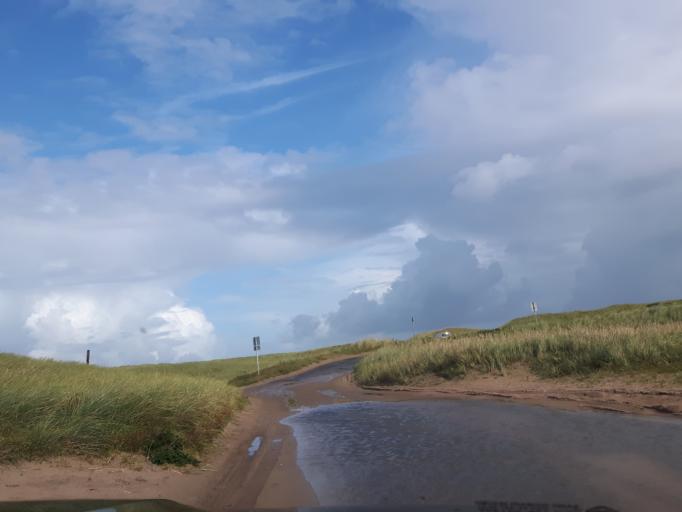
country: DK
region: North Denmark
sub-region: Thisted Kommune
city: Hanstholm
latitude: 57.0864
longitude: 8.5588
